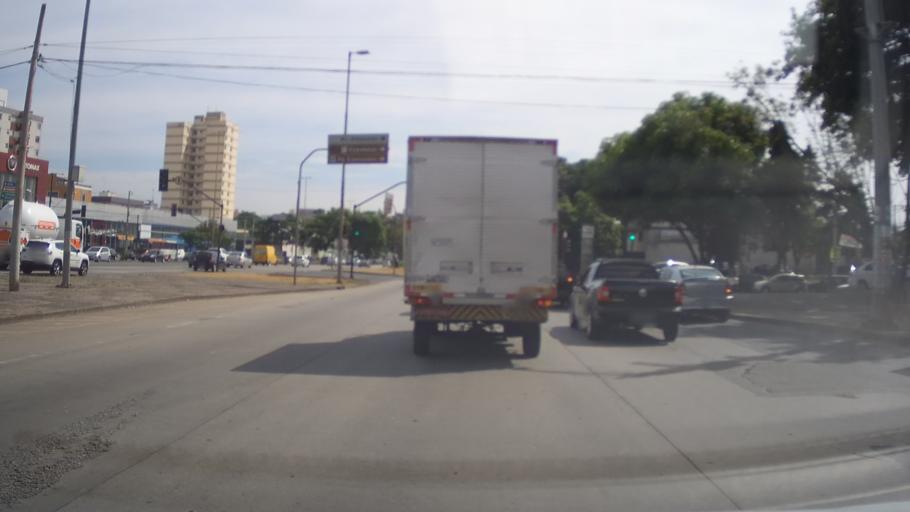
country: BR
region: Minas Gerais
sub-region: Belo Horizonte
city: Belo Horizonte
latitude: -19.9270
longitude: -43.9876
